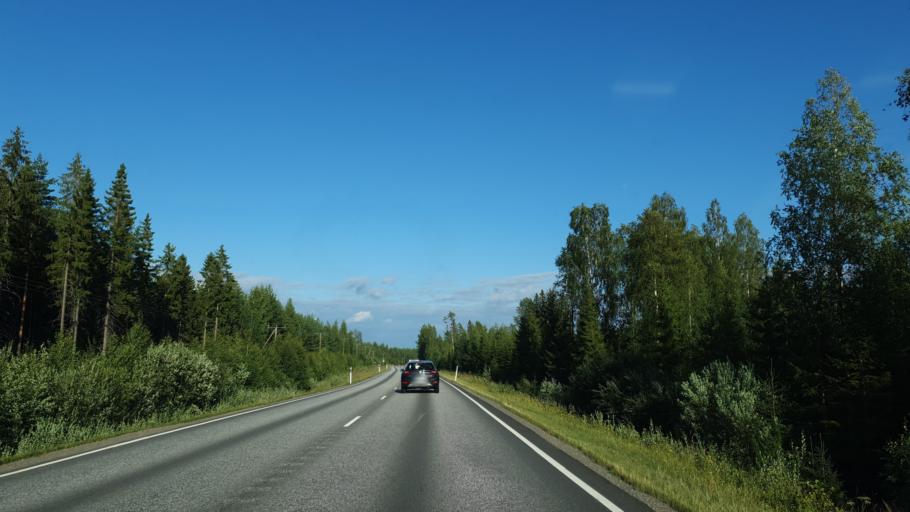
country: FI
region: North Karelia
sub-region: Joensuu
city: Outokumpu
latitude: 62.5329
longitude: 28.9628
